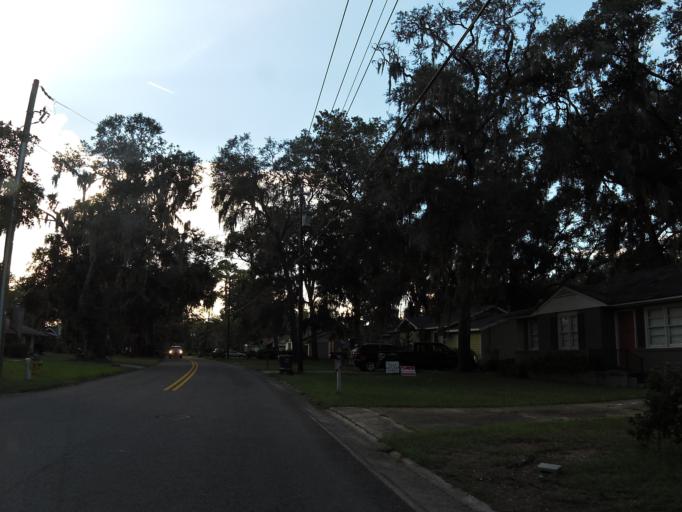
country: US
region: Georgia
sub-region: Camden County
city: St. Marys
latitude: 30.7389
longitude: -81.5594
